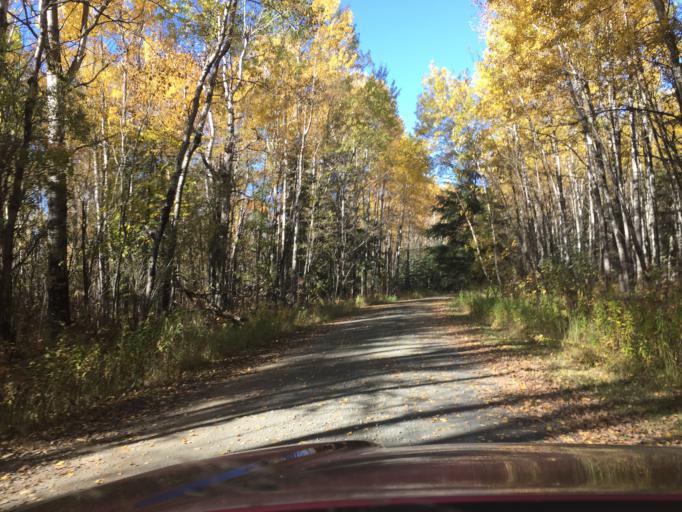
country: US
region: Minnesota
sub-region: Lake of the Woods County
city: Baudette
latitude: 48.2849
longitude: -94.5614
